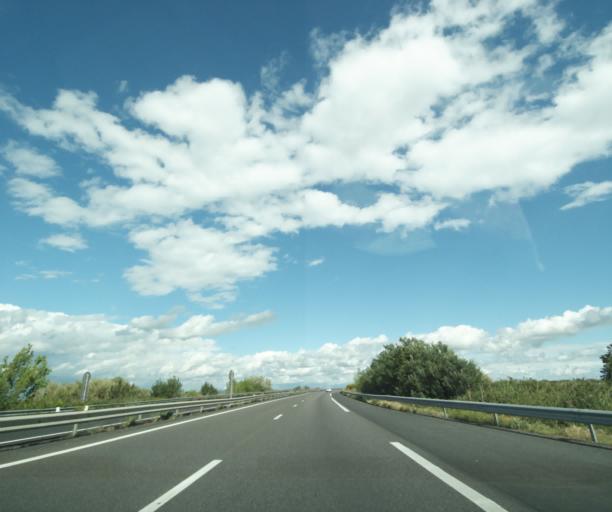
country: FR
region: Languedoc-Roussillon
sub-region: Departement du Gard
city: Bellegarde
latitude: 43.7302
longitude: 4.4919
